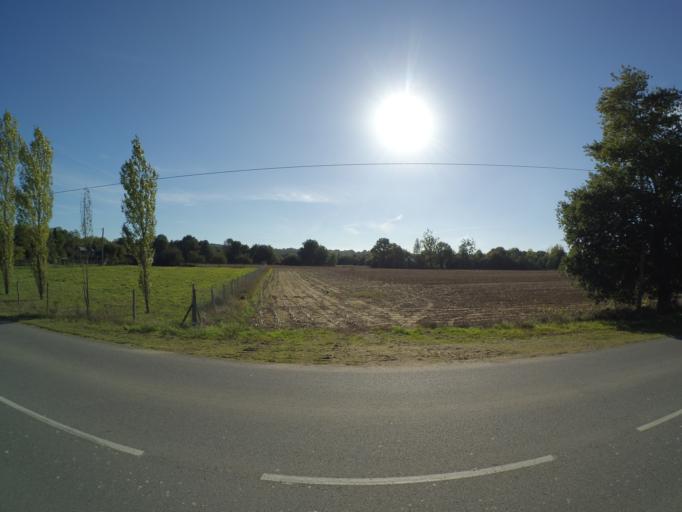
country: FR
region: Brittany
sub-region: Departement du Morbihan
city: Peillac
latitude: 47.7356
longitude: -2.2169
